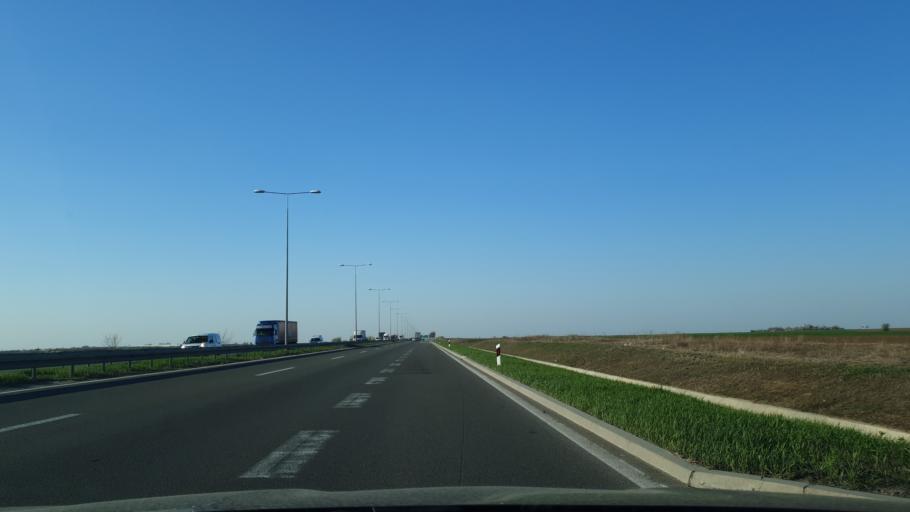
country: RS
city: Dobanovci
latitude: 44.8128
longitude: 20.2535
